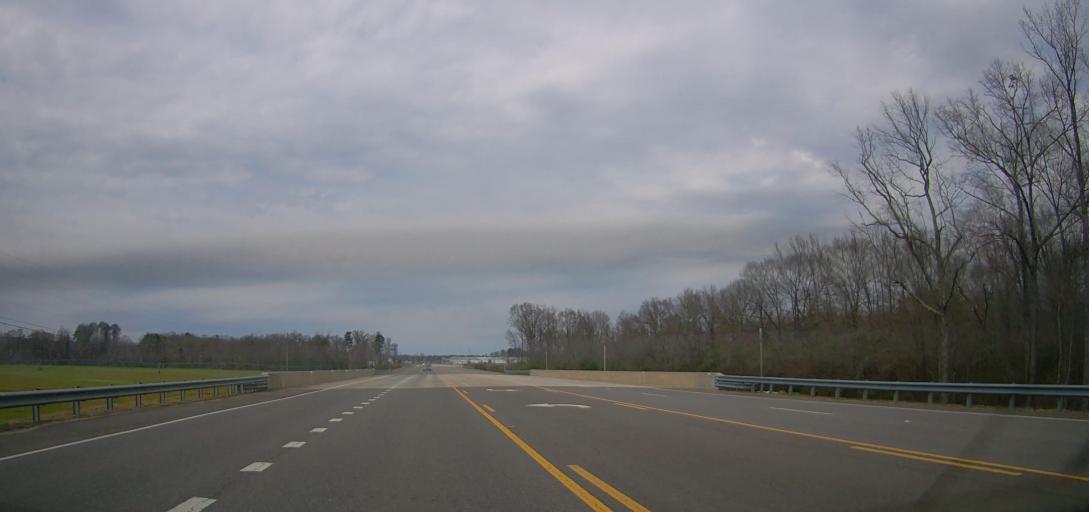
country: US
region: Alabama
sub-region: Marion County
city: Hamilton
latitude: 34.1026
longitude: -87.9891
